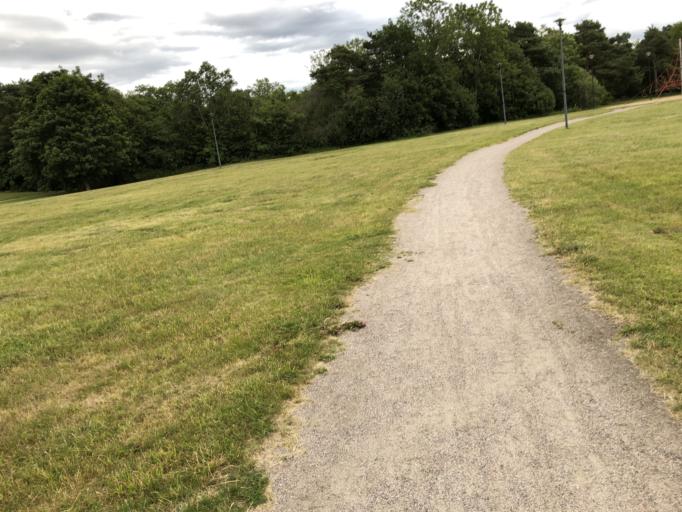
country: EE
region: Harju
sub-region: Viimsi vald
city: Viimsi
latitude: 59.4604
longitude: 24.8307
